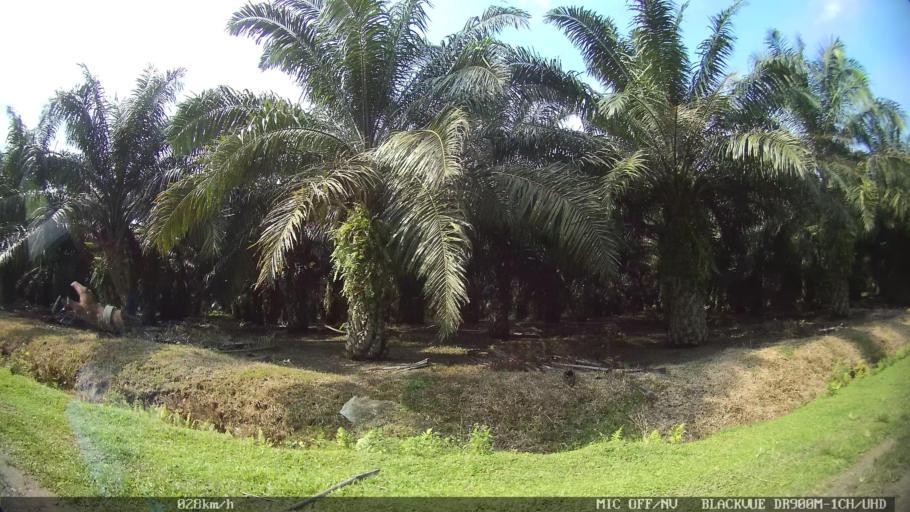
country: ID
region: North Sumatra
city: Binjai
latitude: 3.6428
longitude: 98.5207
